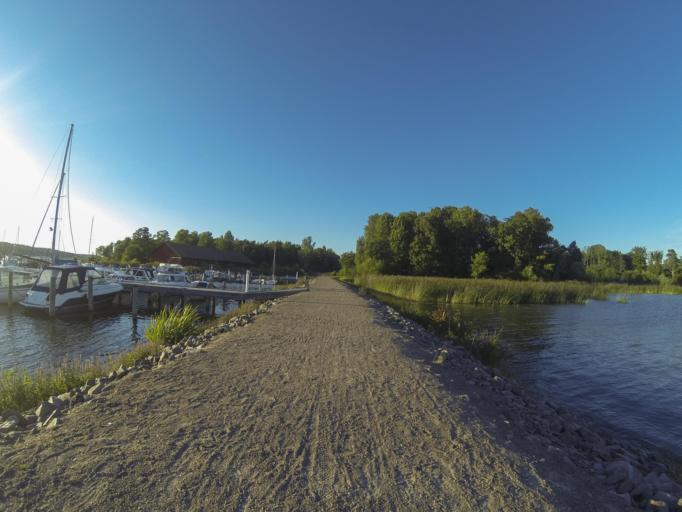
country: SE
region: Vaestmanland
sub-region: Vasteras
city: Vasteras
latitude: 59.5477
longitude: 16.6586
